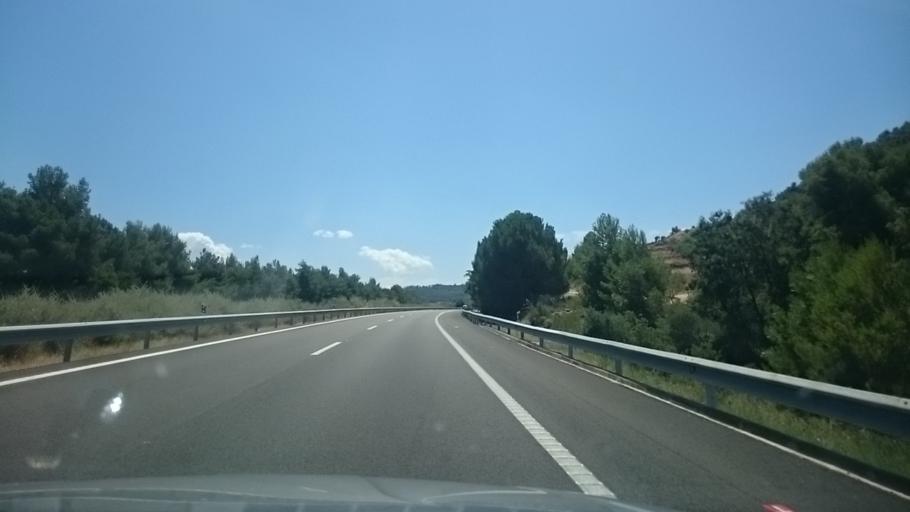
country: ES
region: Catalonia
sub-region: Provincia de Lleida
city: Vinaixa
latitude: 41.4519
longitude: 0.8988
